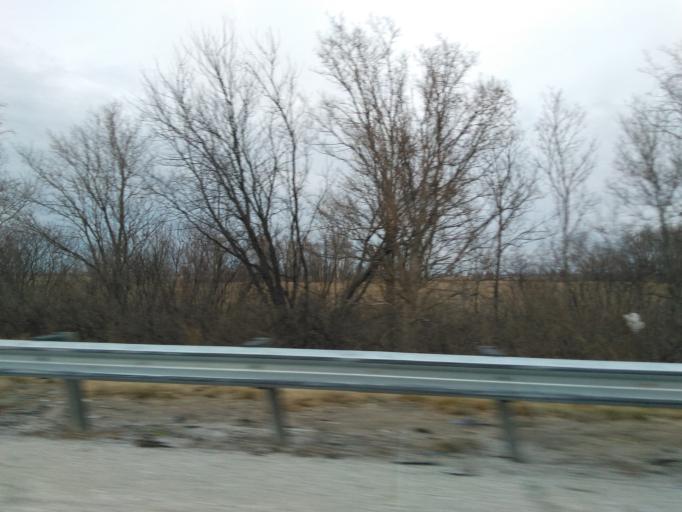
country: US
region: Missouri
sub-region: Saint Louis County
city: Oakville
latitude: 38.4804
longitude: -90.2540
